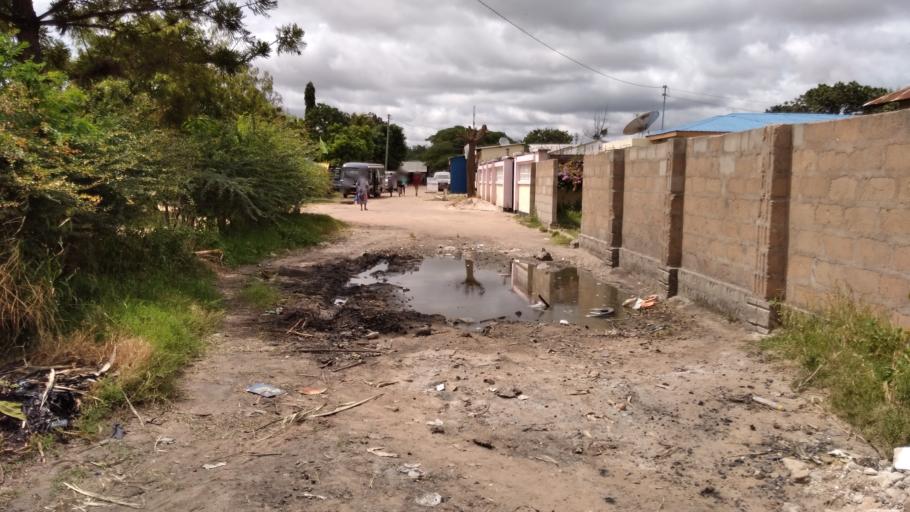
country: TZ
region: Dodoma
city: Dodoma
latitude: -6.1709
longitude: 35.7397
